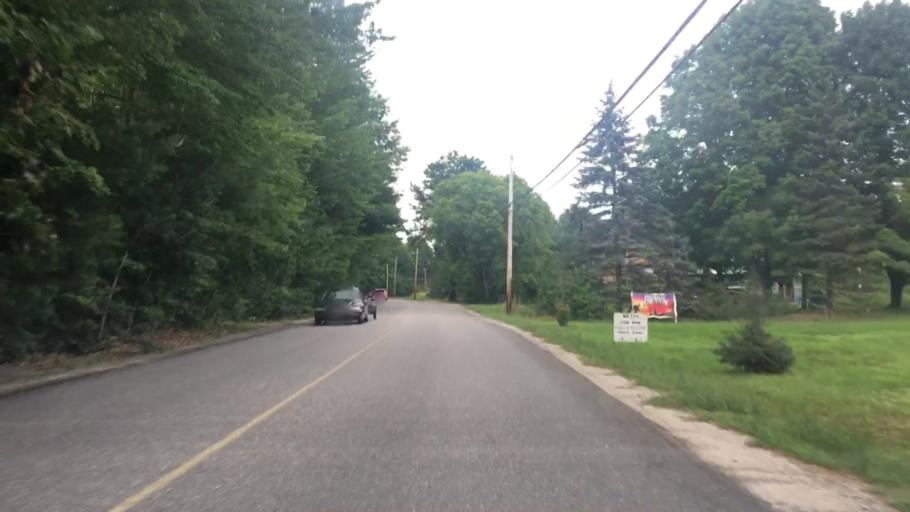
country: US
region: Maine
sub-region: York County
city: Dayton
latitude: 43.5340
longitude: -70.5819
